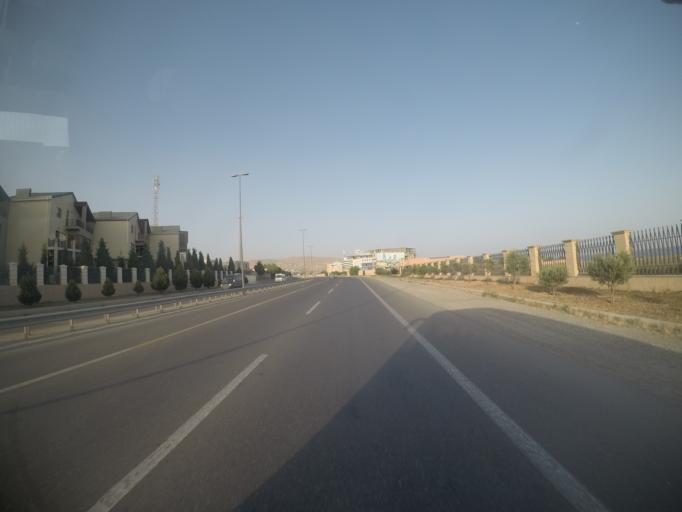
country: AZ
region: Baki
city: Badamdar
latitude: 40.3051
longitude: 49.7885
